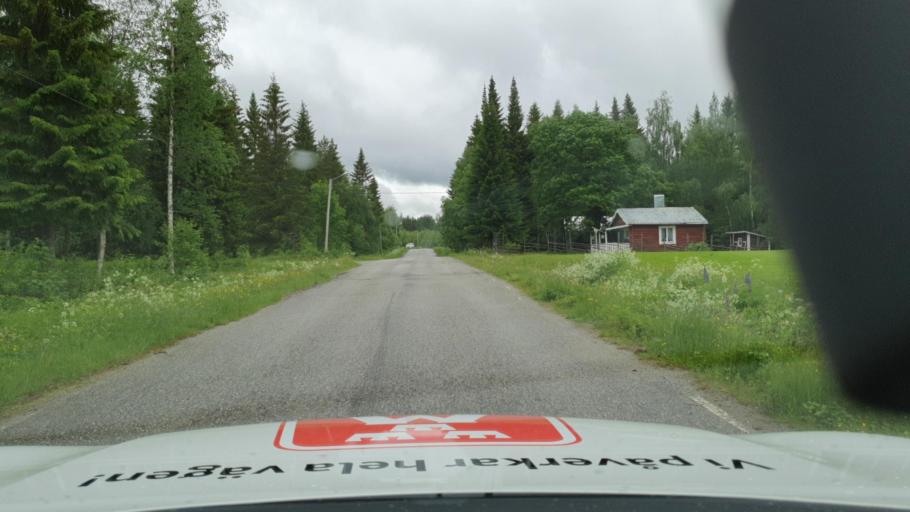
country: SE
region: Vaesterbotten
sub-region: Dorotea Kommun
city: Dorotea
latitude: 64.0944
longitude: 16.6541
